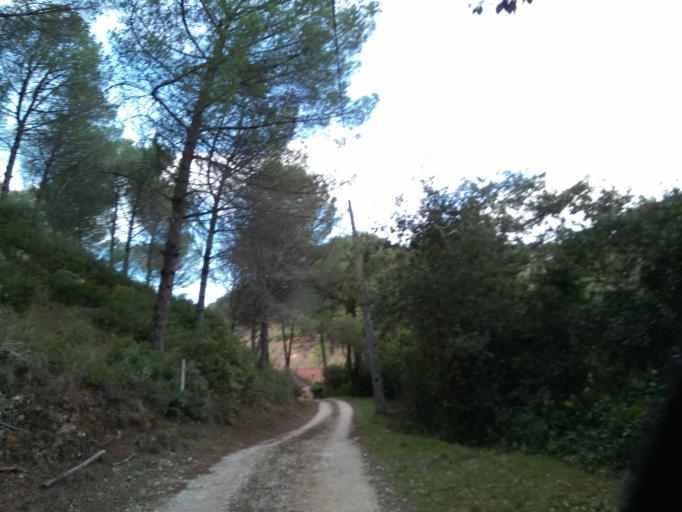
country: PT
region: Leiria
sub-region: Porto de Mos
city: Porto de Mos
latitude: 39.5931
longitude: -8.8103
